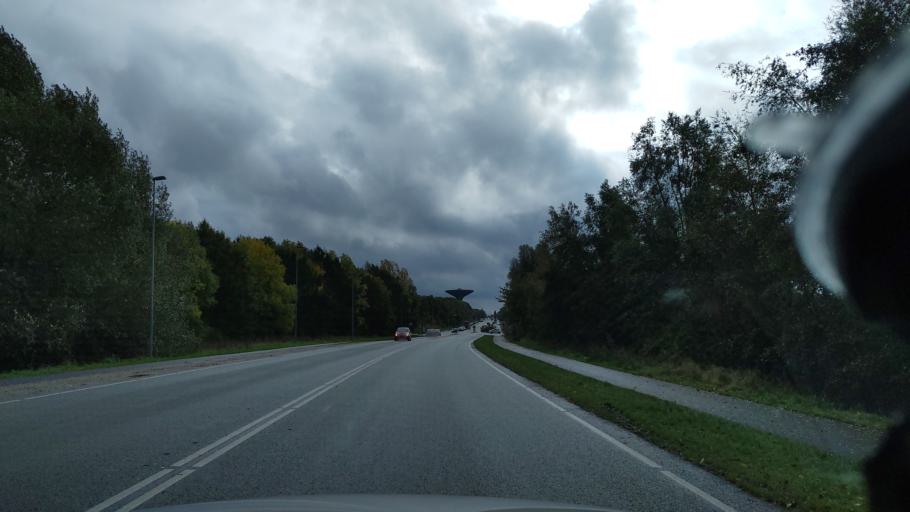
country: DK
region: Zealand
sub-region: Naestved Kommune
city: Naestved
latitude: 55.2412
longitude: 11.7774
